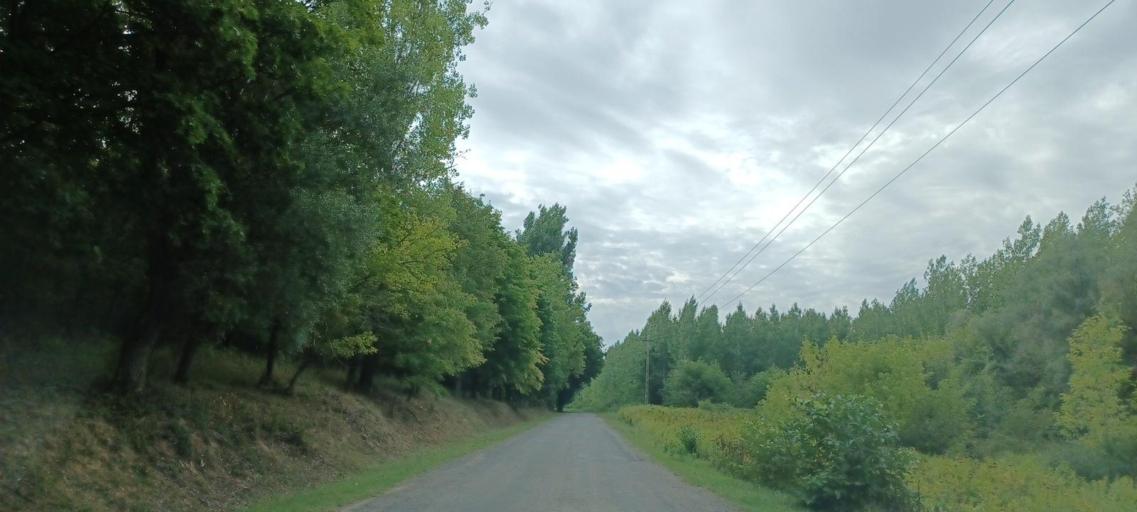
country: HU
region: Tolna
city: Szentgalpuszta
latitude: 46.3503
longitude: 18.6190
